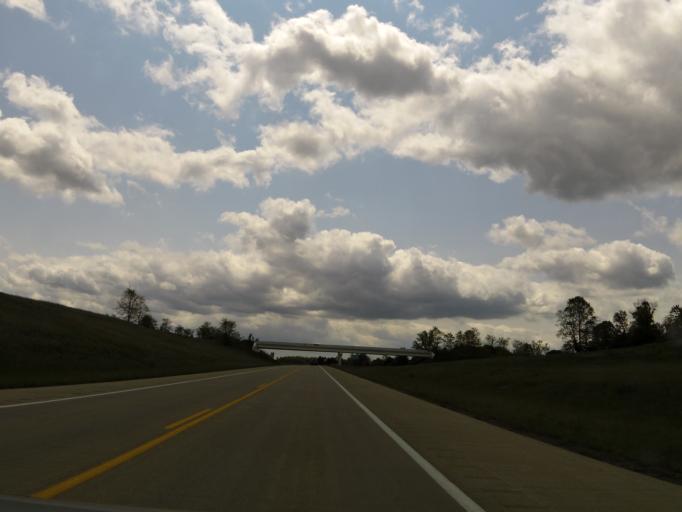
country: US
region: Ohio
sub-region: Athens County
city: Athens
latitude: 39.2586
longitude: -82.0828
